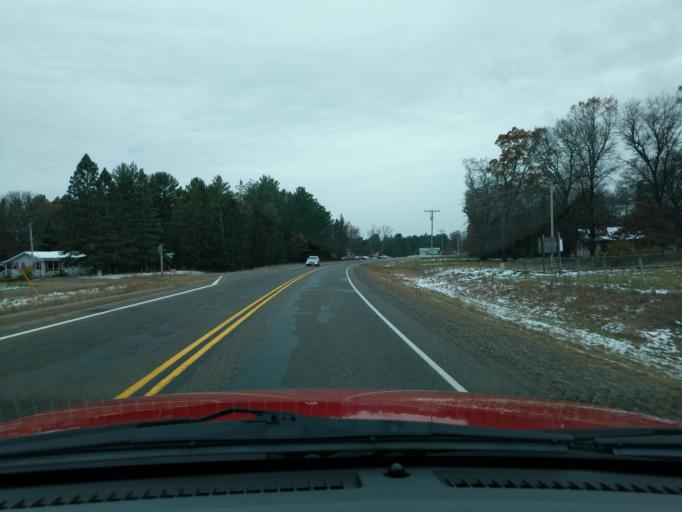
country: US
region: Wisconsin
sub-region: Burnett County
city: Siren
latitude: 45.8170
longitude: -92.3415
